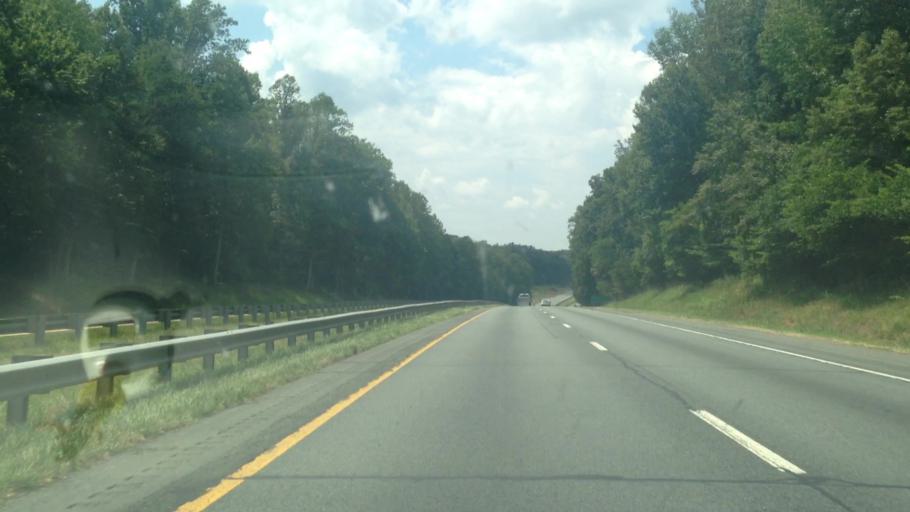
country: US
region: North Carolina
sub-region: Forsyth County
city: Tobaccoville
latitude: 36.2356
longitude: -80.3370
